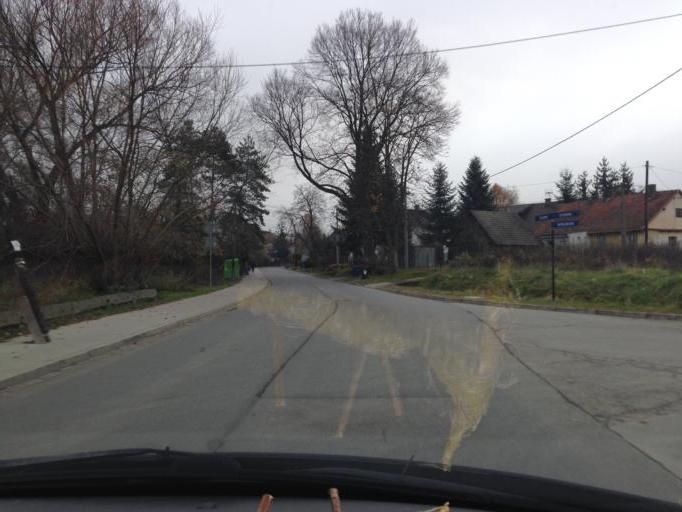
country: PL
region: Lesser Poland Voivodeship
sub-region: Powiat krakowski
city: Wrzasowice
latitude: 50.0050
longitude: 19.9460
